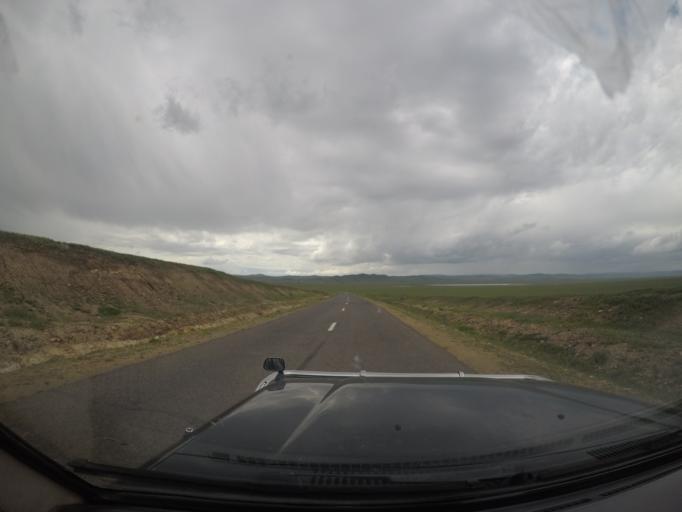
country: MN
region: Hentiy
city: Avraga
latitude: 47.4758
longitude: 109.5229
